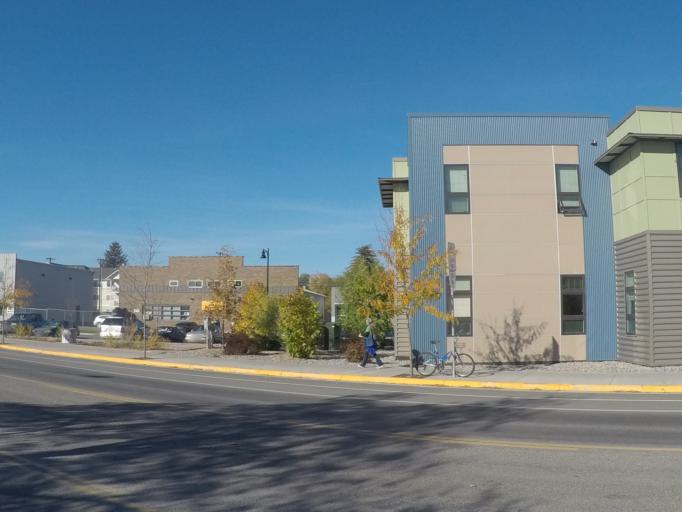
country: US
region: Montana
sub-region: Missoula County
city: Missoula
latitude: 46.8766
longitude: -114.0093
